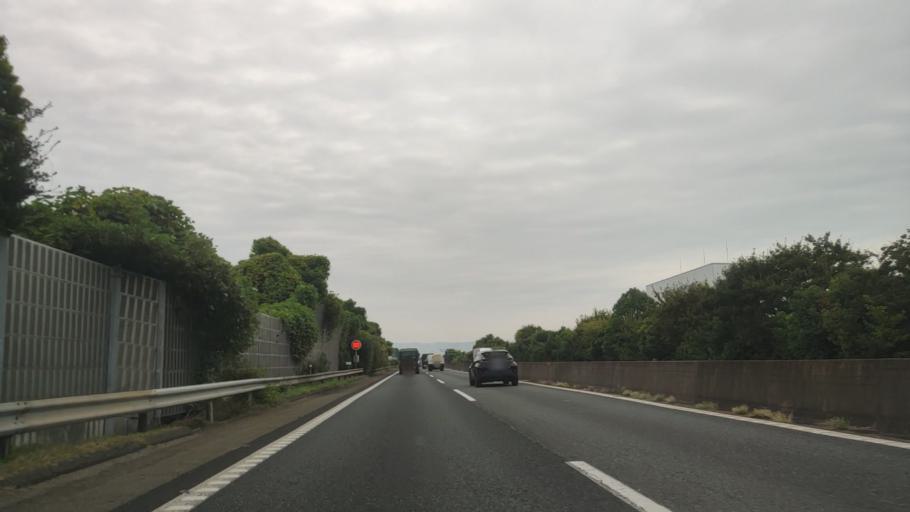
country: JP
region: Nara
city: Tawaramoto
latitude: 34.5978
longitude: 135.7515
